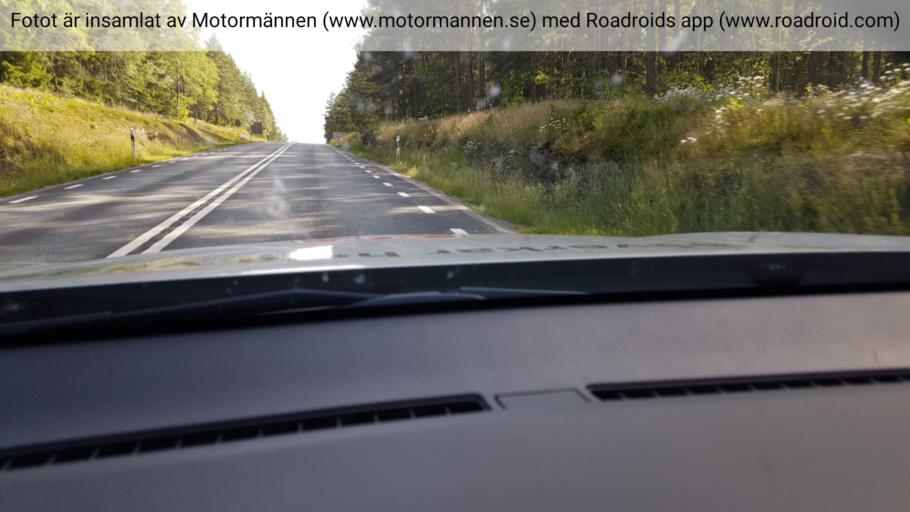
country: SE
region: Joenkoeping
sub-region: Aneby Kommun
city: Aneby
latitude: 57.8713
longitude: 14.8696
